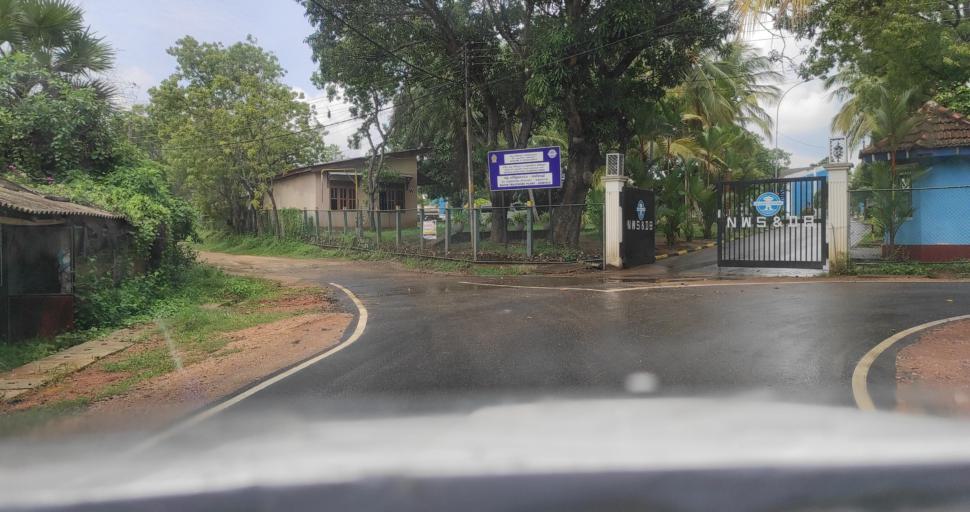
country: LK
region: Eastern Province
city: Trincomalee
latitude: 8.3756
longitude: 81.0054
